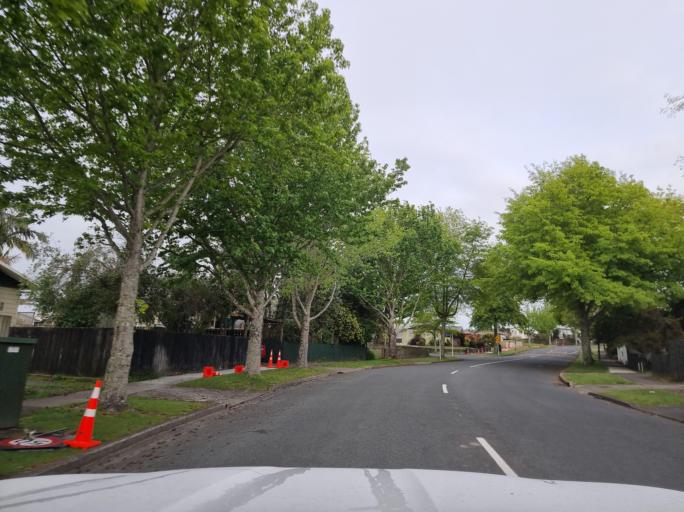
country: NZ
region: Northland
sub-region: Whangarei
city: Whangarei
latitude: -35.7518
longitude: 174.3626
